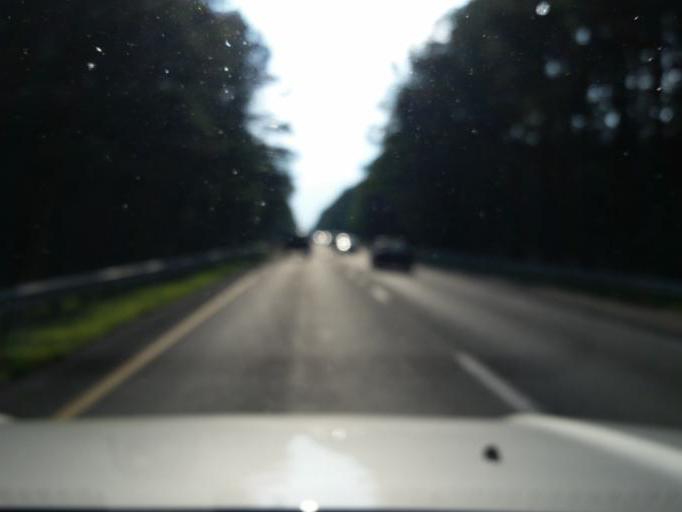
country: US
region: Virginia
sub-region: New Kent County
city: New Kent
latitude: 37.4827
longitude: -76.9337
